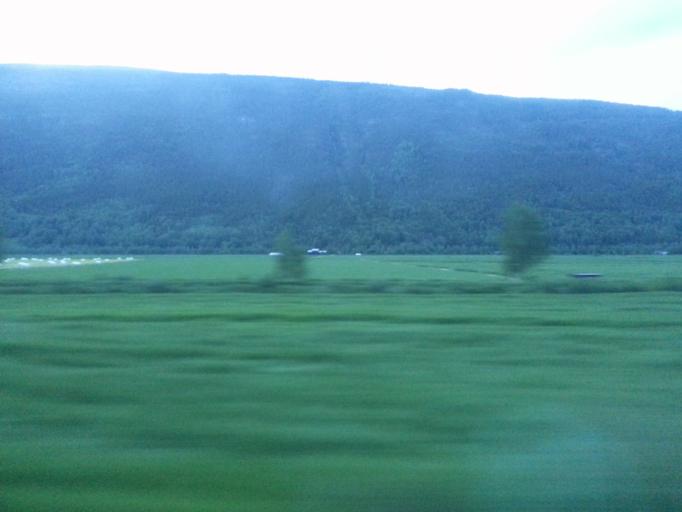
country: NO
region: Oppland
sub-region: Sel
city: Otta
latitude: 61.8174
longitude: 9.5231
